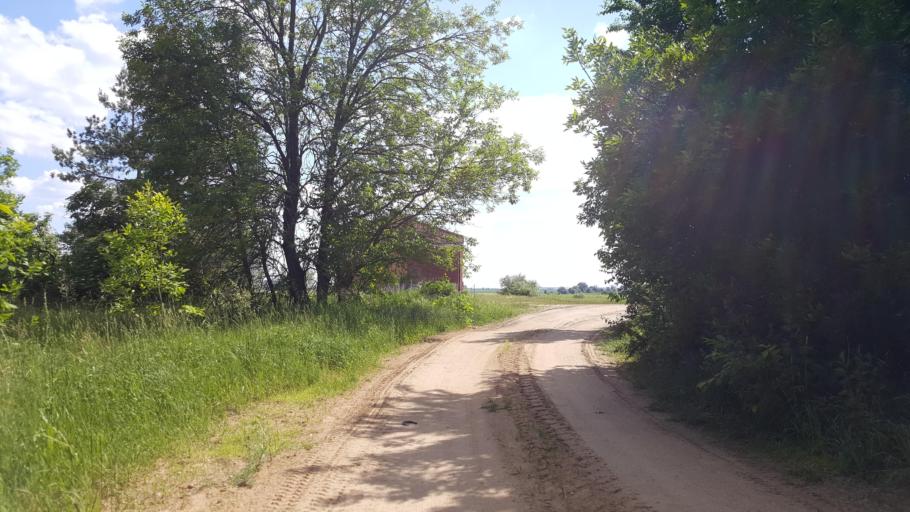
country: BY
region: Brest
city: Kamyanyuki
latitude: 52.5012
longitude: 23.7045
